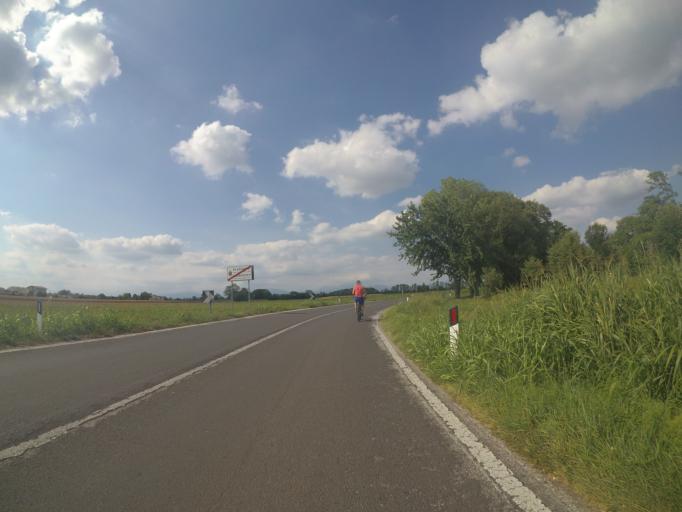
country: IT
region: Friuli Venezia Giulia
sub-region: Provincia di Udine
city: San Vito di Fagagna
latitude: 46.0712
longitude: 13.0830
